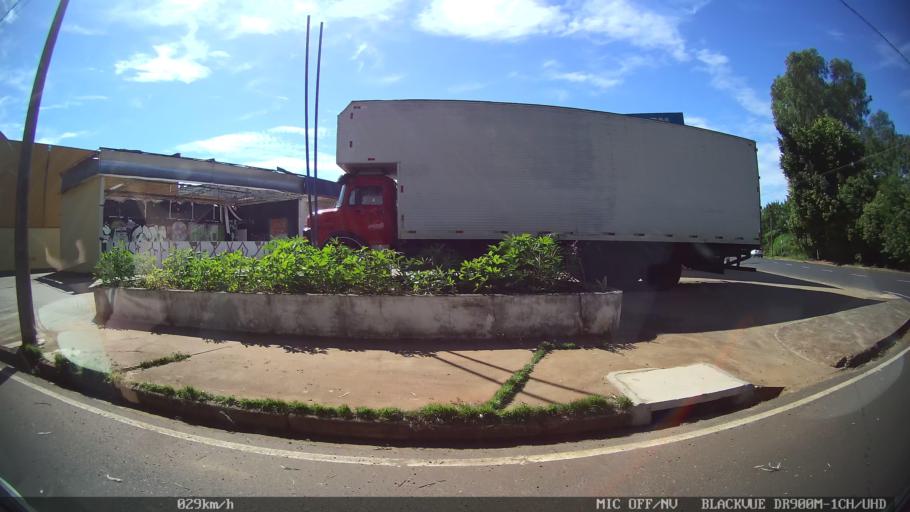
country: BR
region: Sao Paulo
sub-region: Sao Jose Do Rio Preto
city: Sao Jose do Rio Preto
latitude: -20.8443
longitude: -49.3587
